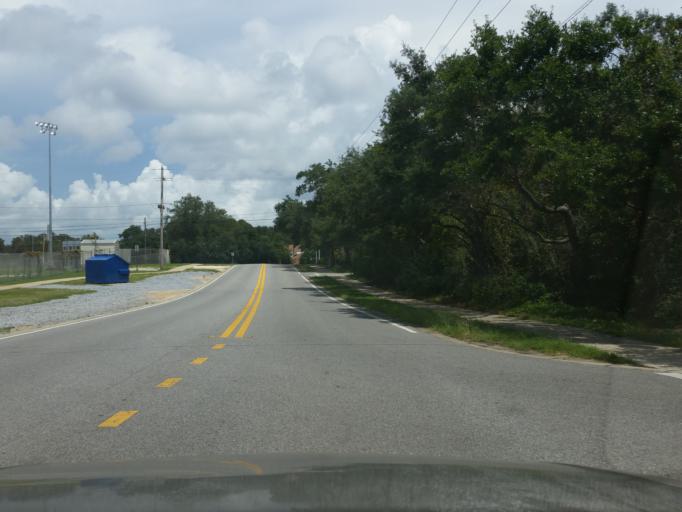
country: US
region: Florida
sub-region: Santa Rosa County
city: Gulf Breeze
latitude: 30.3622
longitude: -87.1663
